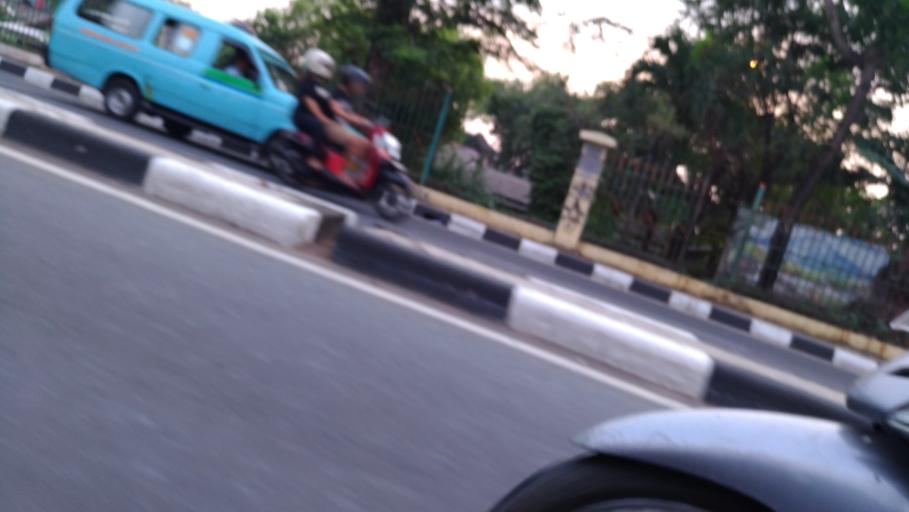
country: ID
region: West Java
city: Depok
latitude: -6.3234
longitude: 106.8647
